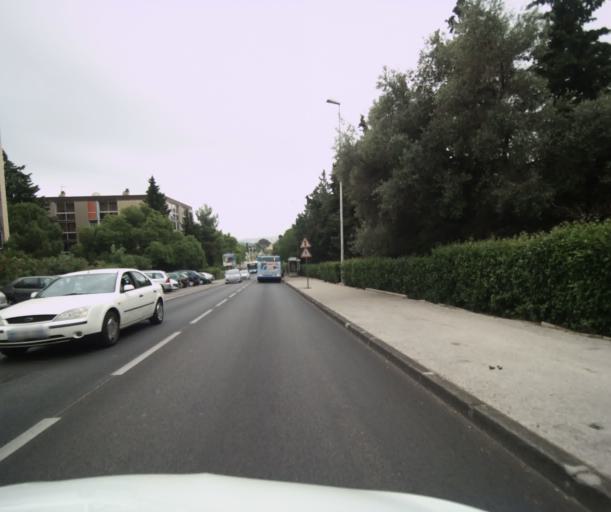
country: FR
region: Provence-Alpes-Cote d'Azur
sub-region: Departement du Var
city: La Seyne-sur-Mer
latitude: 43.1307
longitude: 5.8819
